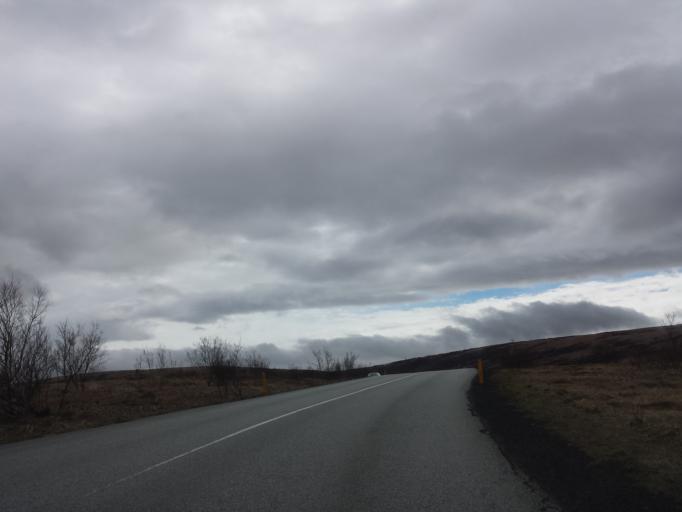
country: IS
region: Capital Region
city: Gardabaer
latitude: 64.0829
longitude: -21.8818
